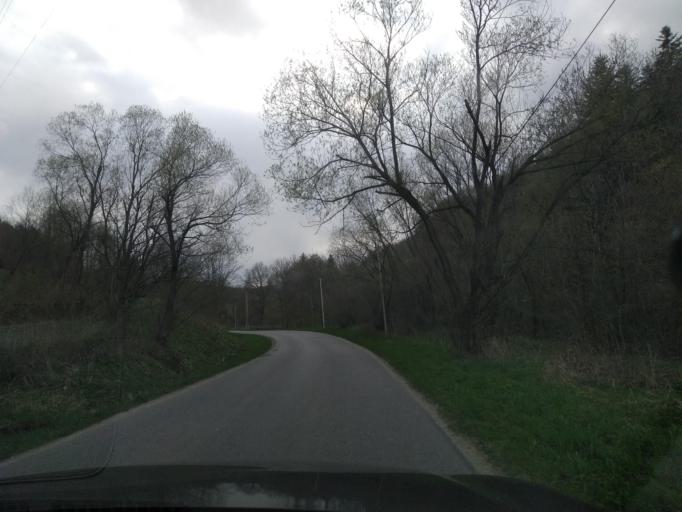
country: PL
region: Subcarpathian Voivodeship
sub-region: Powiat leski
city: Baligrod
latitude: 49.3487
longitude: 22.2516
